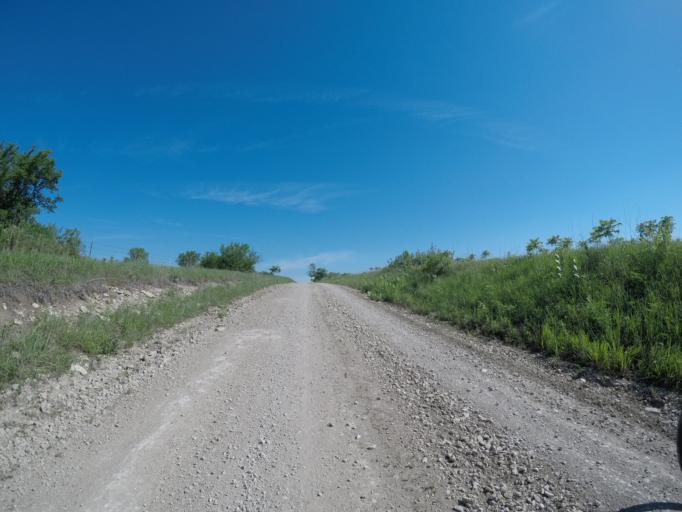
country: US
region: Kansas
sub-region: Wabaunsee County
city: Alma
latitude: 38.9457
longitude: -96.1138
